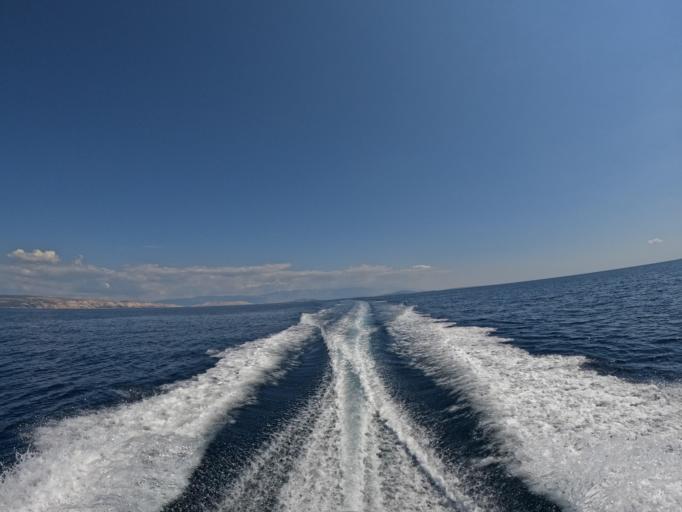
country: HR
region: Primorsko-Goranska
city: Cres
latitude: 44.9336
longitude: 14.5158
